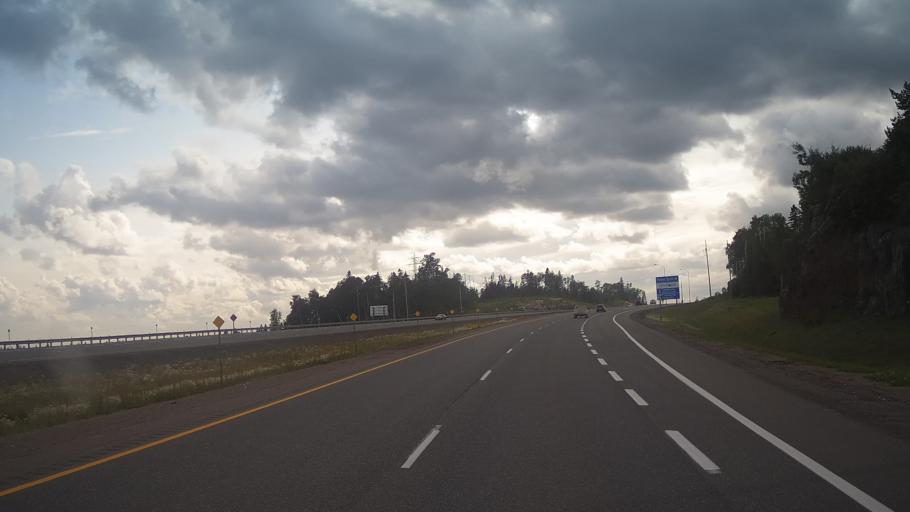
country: CA
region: Ontario
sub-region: Thunder Bay District
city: Thunder Bay
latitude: 48.4842
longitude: -89.1670
